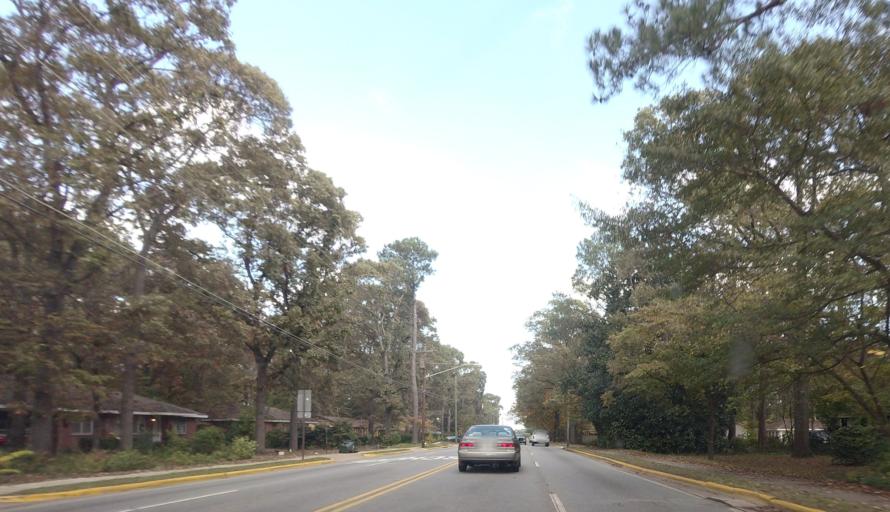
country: US
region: Georgia
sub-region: Houston County
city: Warner Robins
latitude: 32.6263
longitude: -83.6257
